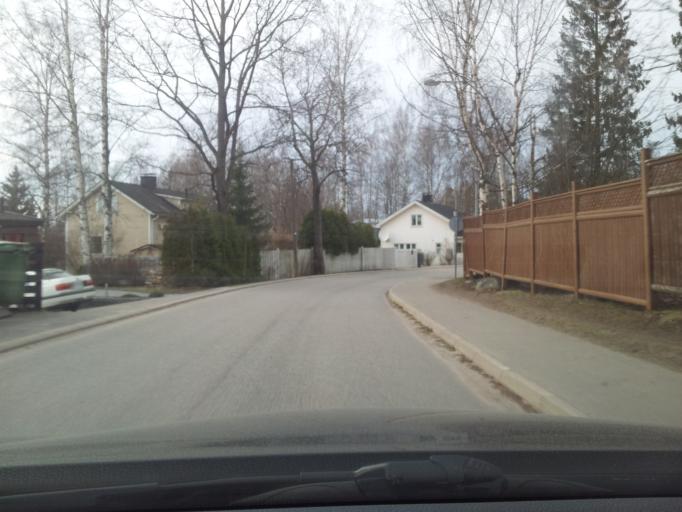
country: FI
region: Uusimaa
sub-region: Helsinki
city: Kauniainen
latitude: 60.1680
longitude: 24.7093
